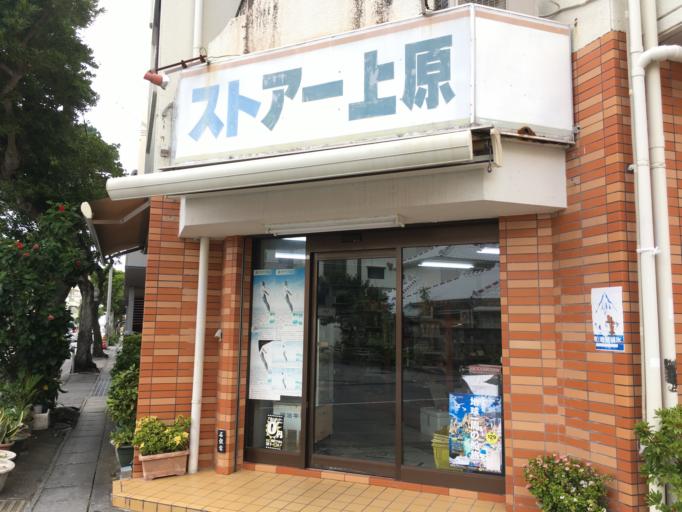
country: JP
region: Okinawa
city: Naha-shi
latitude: 26.2216
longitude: 127.6761
